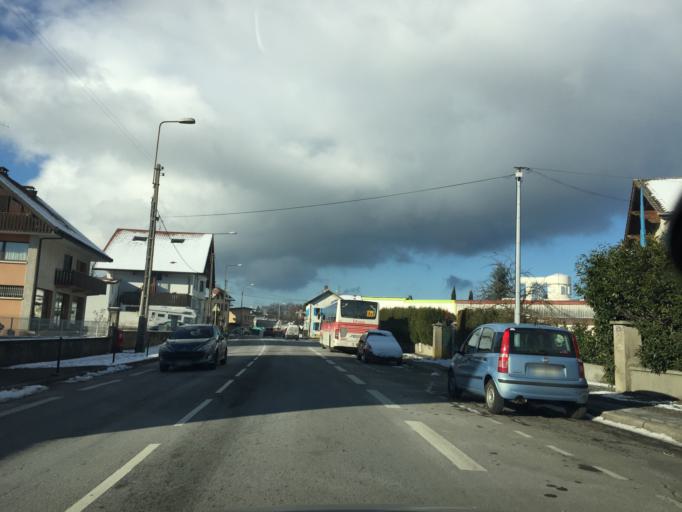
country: FR
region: Rhone-Alpes
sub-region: Departement de la Haute-Savoie
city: Thonon-les-Bains
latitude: 46.3694
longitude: 6.4986
